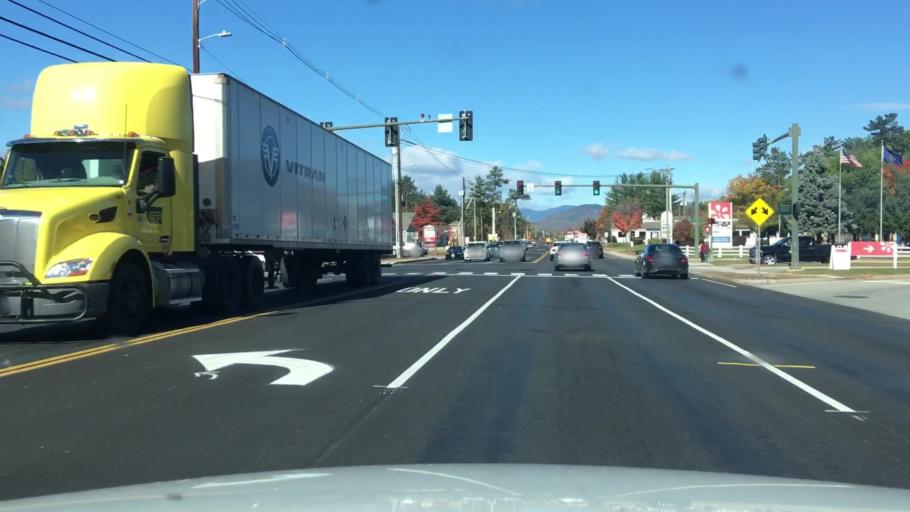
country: US
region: New Hampshire
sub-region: Carroll County
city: North Conway
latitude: 44.0225
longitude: -71.1167
